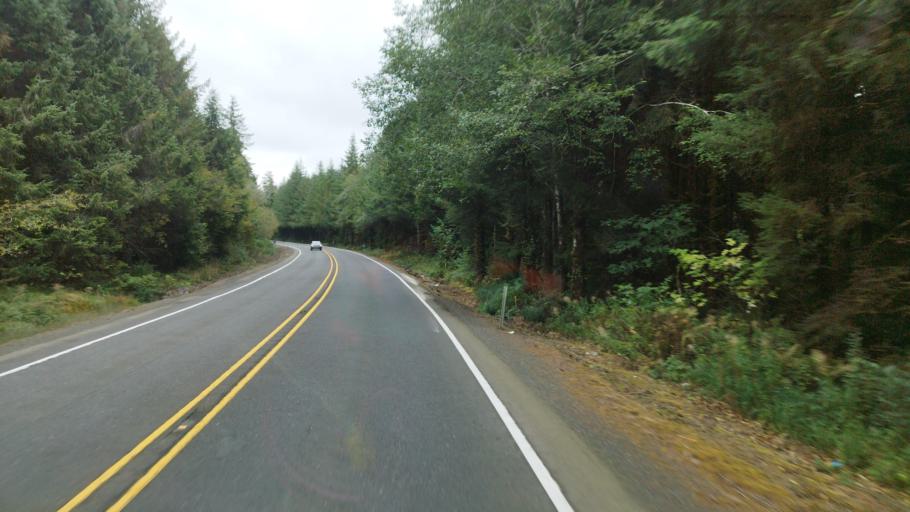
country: US
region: Oregon
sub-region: Clatsop County
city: Cannon Beach
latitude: 45.9010
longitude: -123.8647
